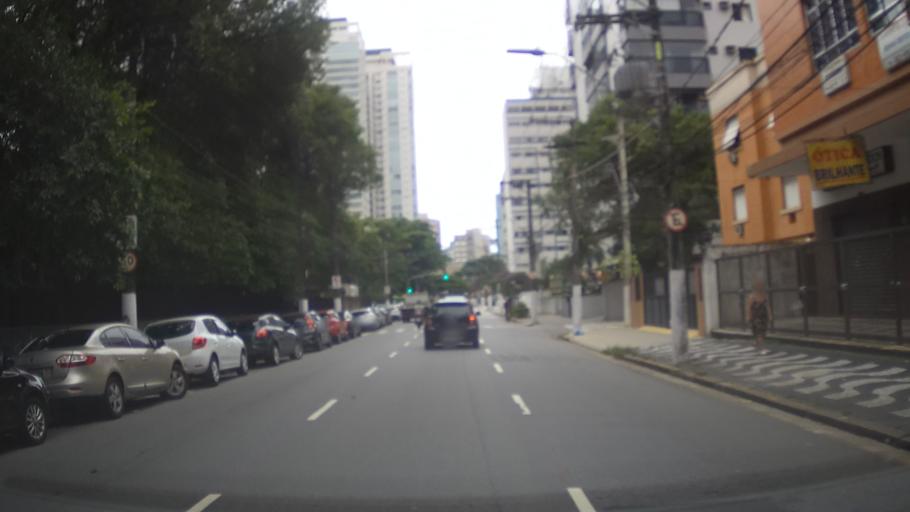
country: BR
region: Sao Paulo
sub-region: Santos
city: Santos
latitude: -23.9779
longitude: -46.3118
